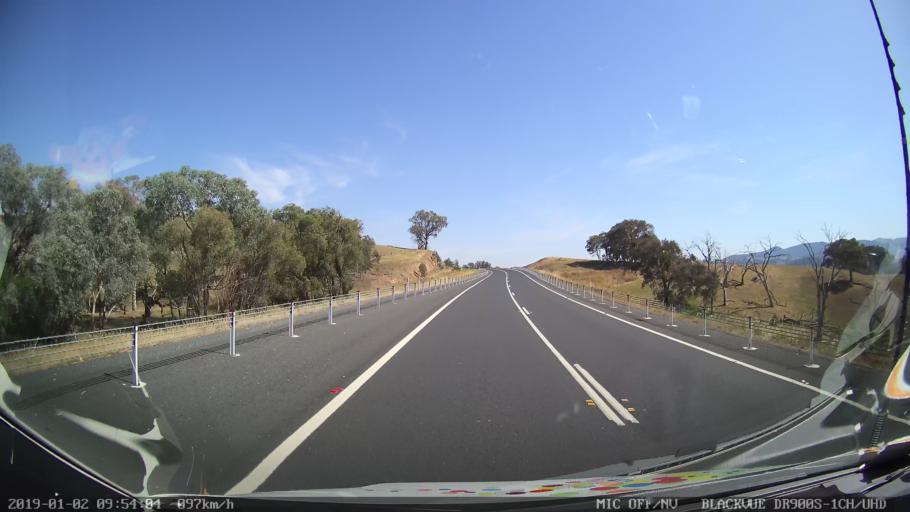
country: AU
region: New South Wales
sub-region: Tumut Shire
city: Tumut
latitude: -35.2401
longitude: 148.1981
